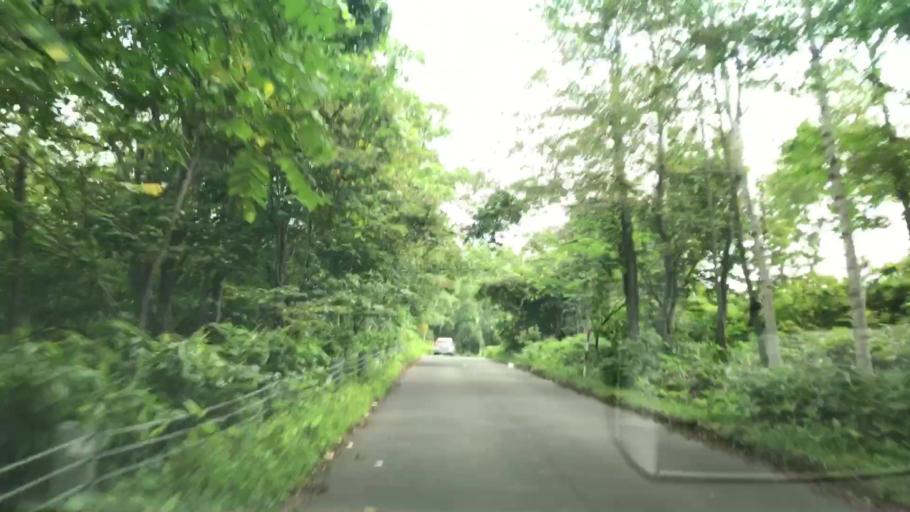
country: JP
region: Hokkaido
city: Yoichi
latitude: 43.1362
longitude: 140.8227
